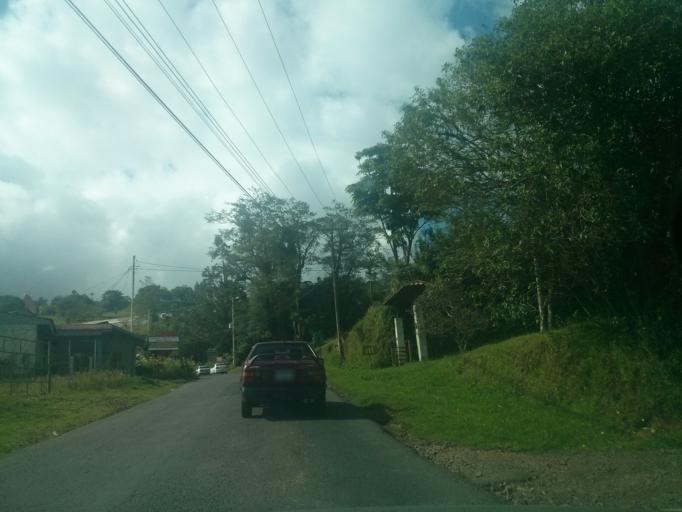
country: CR
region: Alajuela
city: Sabanilla
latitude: 10.1617
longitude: -84.1990
